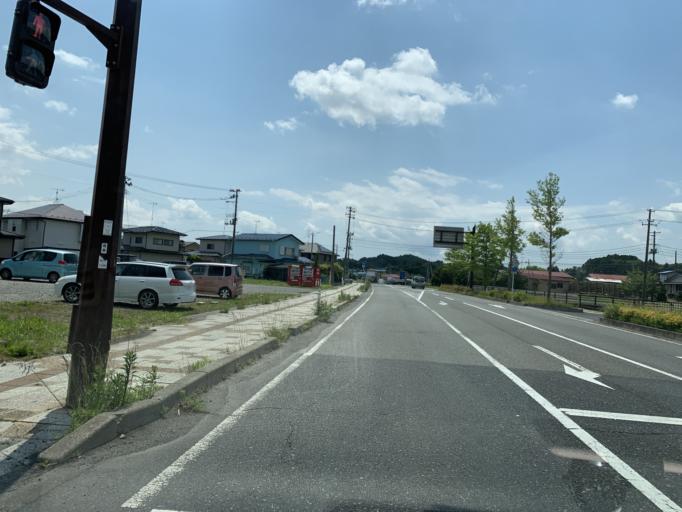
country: JP
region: Miyagi
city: Kogota
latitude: 38.5112
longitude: 141.0667
